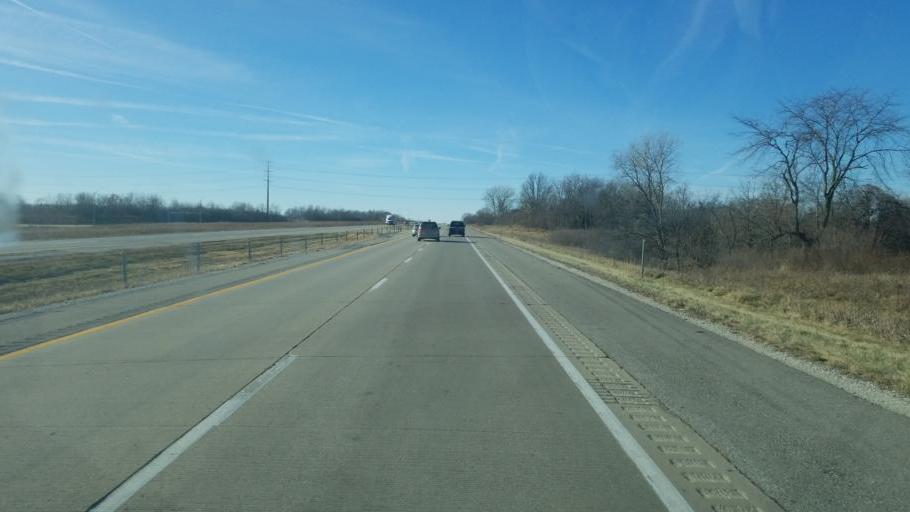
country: US
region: Iowa
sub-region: Dallas County
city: Van Meter
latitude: 41.5561
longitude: -93.9153
